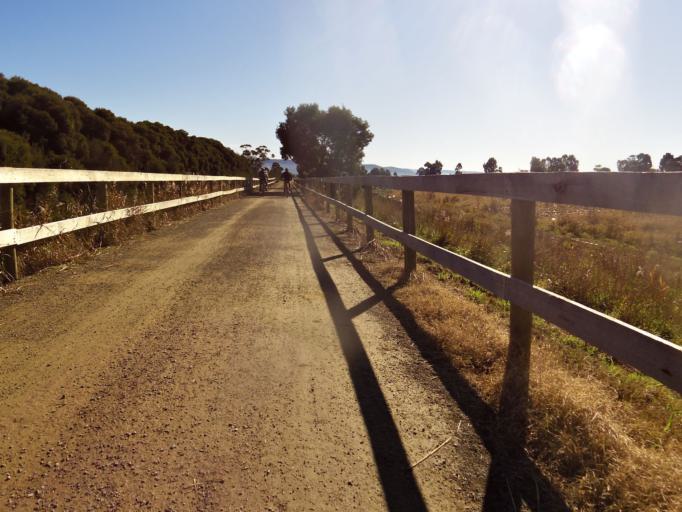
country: AU
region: Victoria
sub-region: Yarra Ranges
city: Lilydale
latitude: -37.7188
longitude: 145.3683
